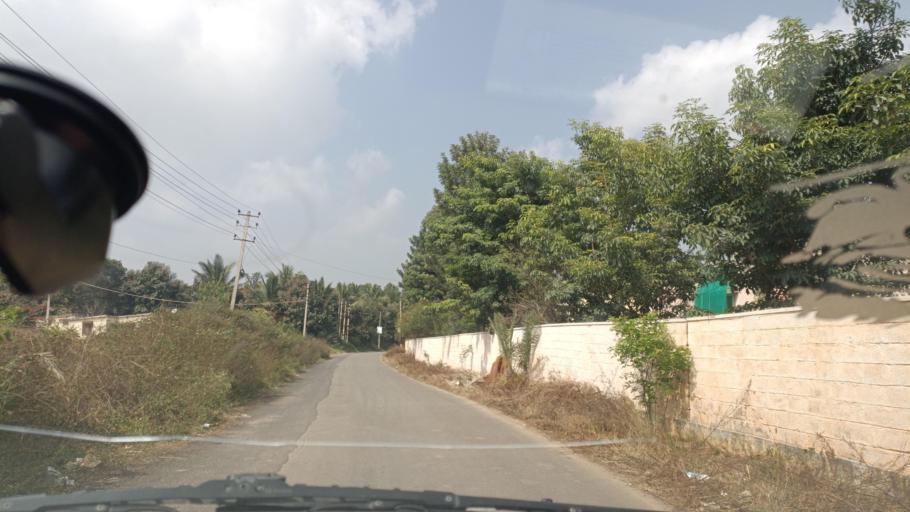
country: IN
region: Karnataka
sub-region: Bangalore Urban
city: Yelahanka
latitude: 13.1507
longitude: 77.6334
